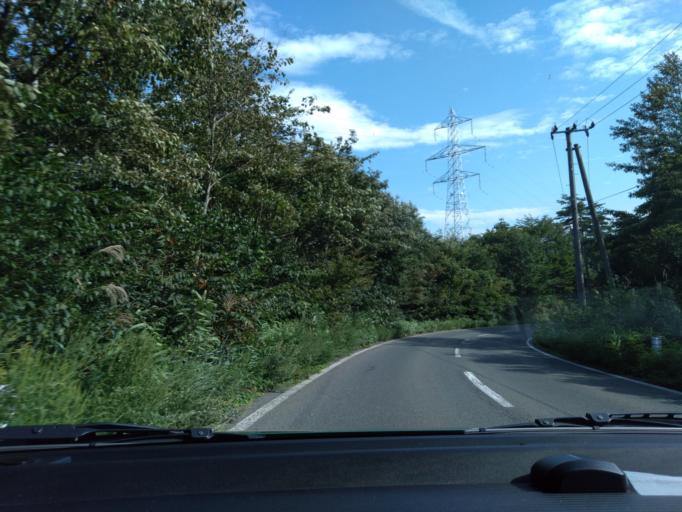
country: JP
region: Iwate
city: Morioka-shi
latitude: 39.6349
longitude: 141.0836
